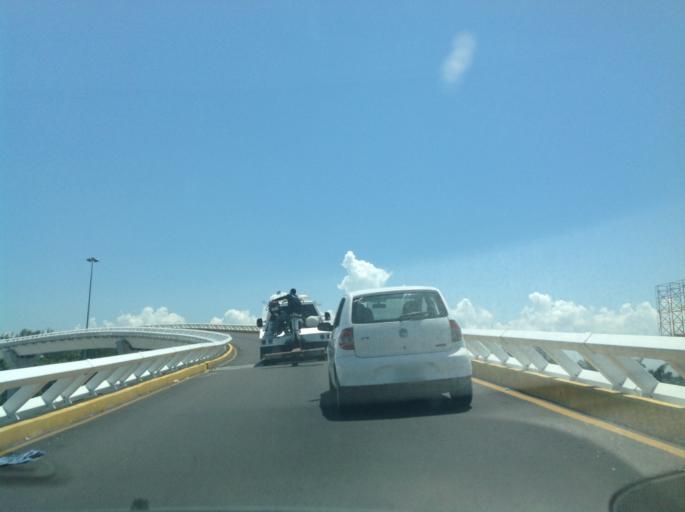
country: MX
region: Veracruz
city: Veracruz
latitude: 19.1475
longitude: -96.1292
